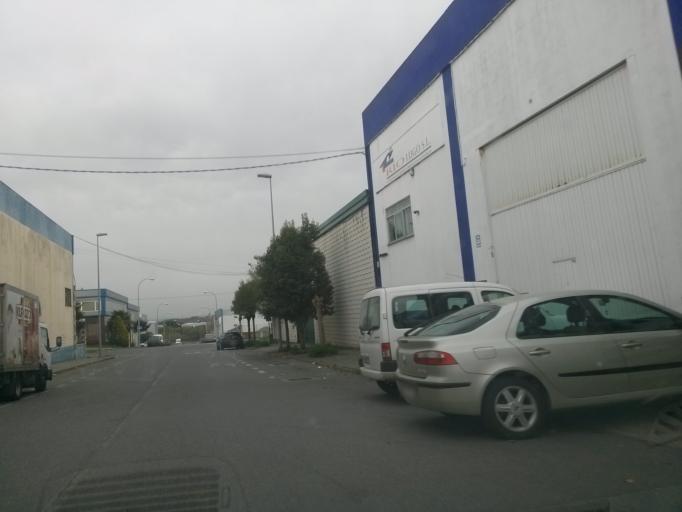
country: ES
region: Galicia
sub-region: Provincia de Lugo
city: Lugo
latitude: 43.0433
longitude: -7.5632
